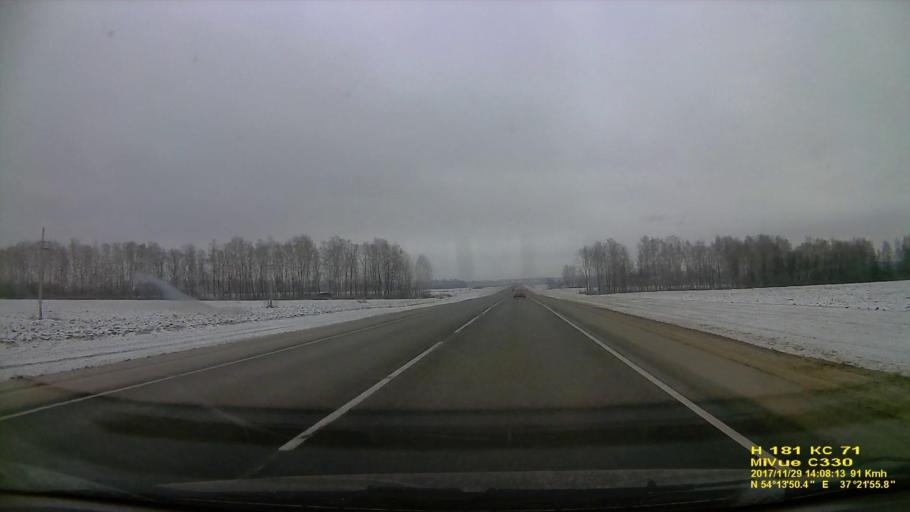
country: RU
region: Tula
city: Leninskiy
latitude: 54.2307
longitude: 37.3656
